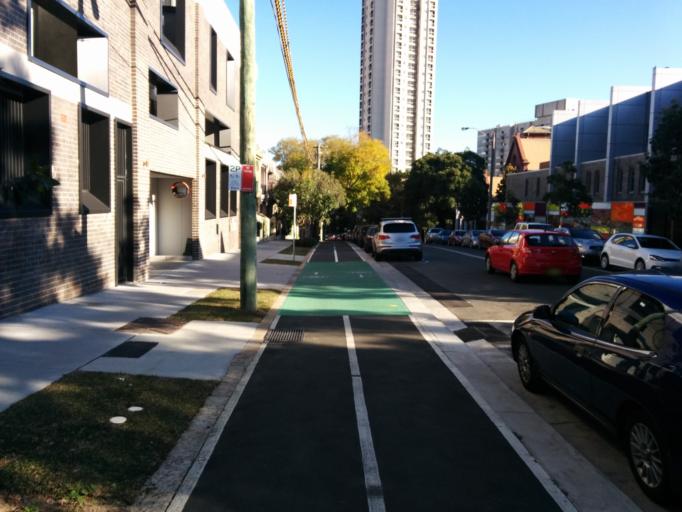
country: AU
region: New South Wales
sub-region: City of Sydney
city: Redfern
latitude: -33.8942
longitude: 151.2019
